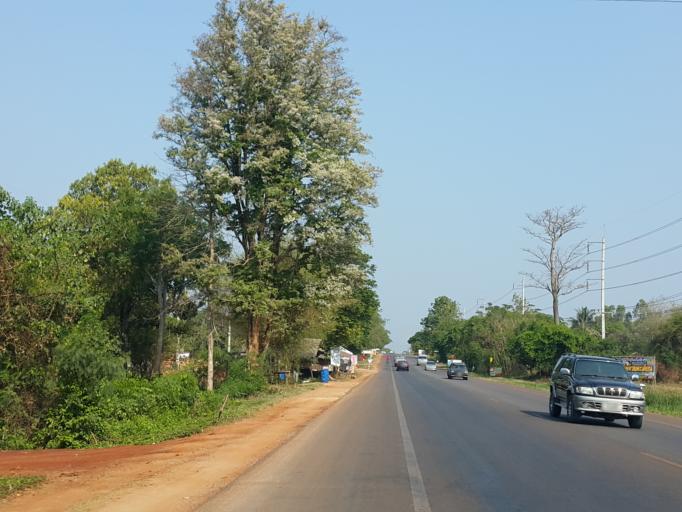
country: TH
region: Kanchanaburi
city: Sai Yok
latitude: 14.1243
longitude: 99.1745
